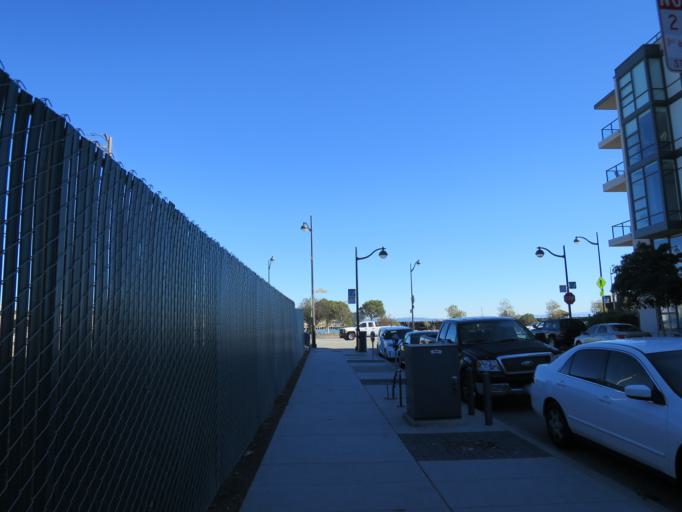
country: US
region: California
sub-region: San Francisco County
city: San Francisco
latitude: 37.7722
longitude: -122.3875
